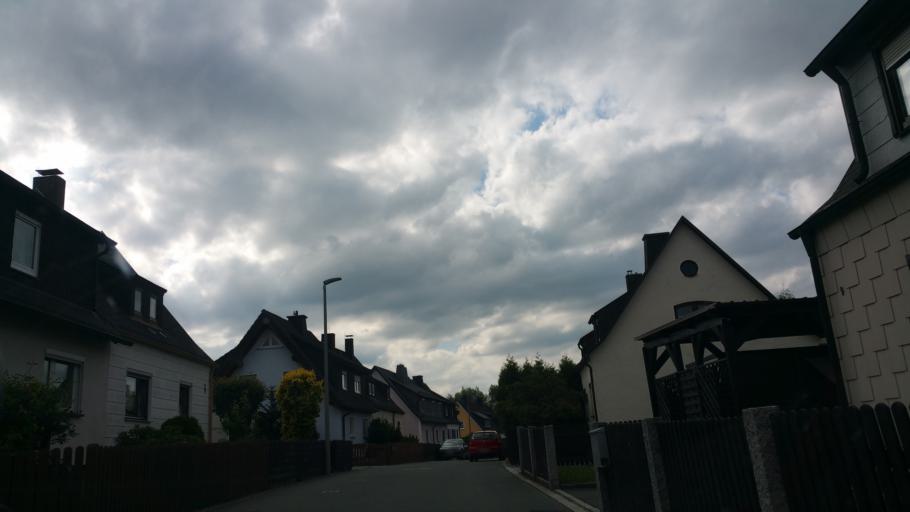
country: DE
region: Bavaria
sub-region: Upper Franconia
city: Rehau
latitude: 50.2378
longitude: 12.0232
